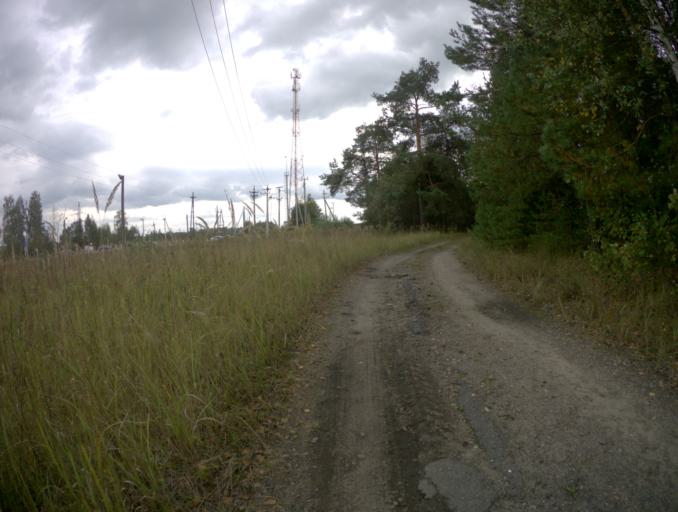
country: RU
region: Vladimir
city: Raduzhnyy
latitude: 56.0234
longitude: 40.3857
